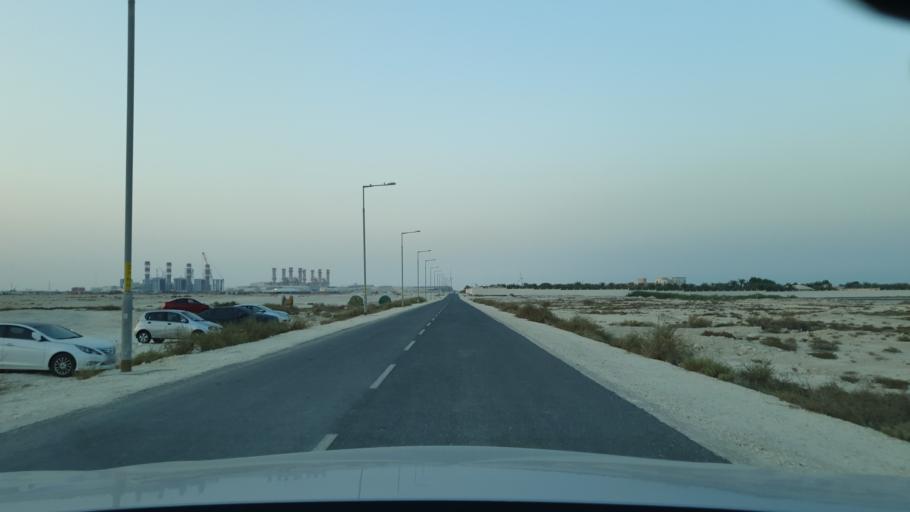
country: BH
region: Central Governorate
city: Dar Kulayb
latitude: 25.9562
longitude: 50.6113
